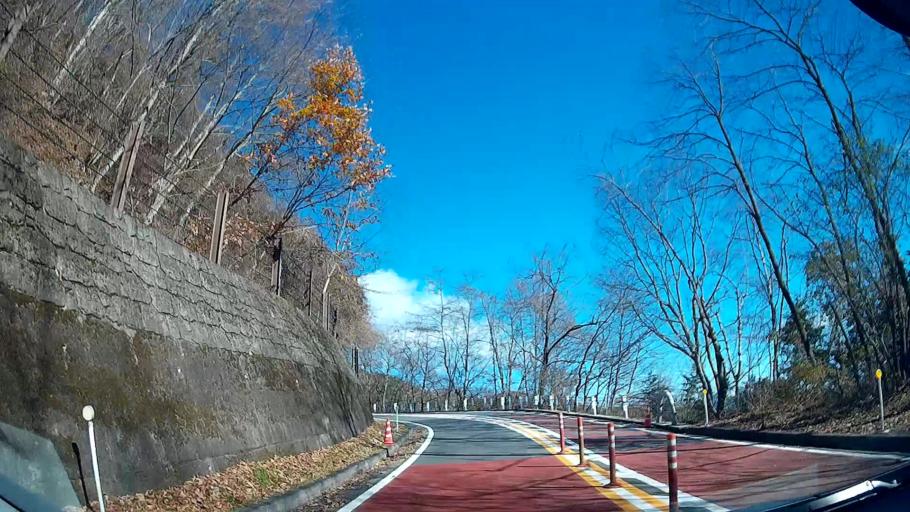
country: JP
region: Yamanashi
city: Uenohara
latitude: 35.7444
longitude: 139.0419
